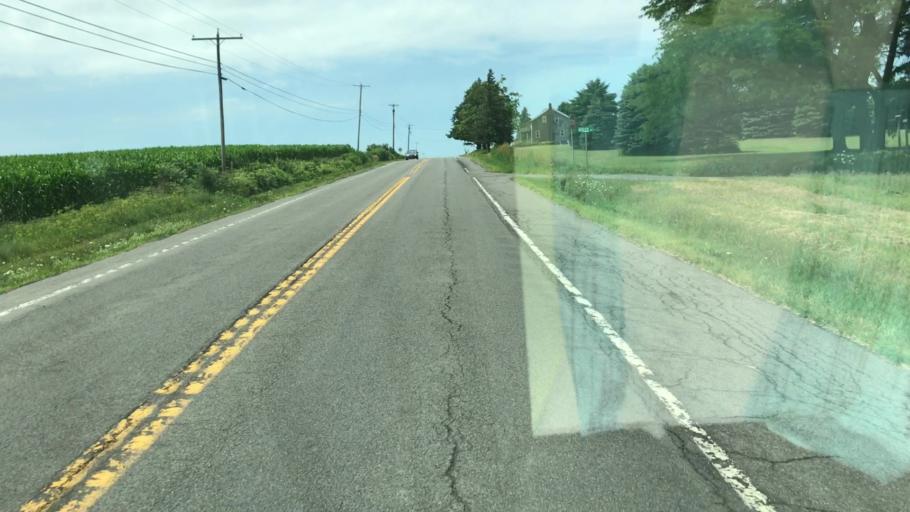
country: US
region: New York
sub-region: Onondaga County
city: Marcellus
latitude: 42.9215
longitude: -76.2577
